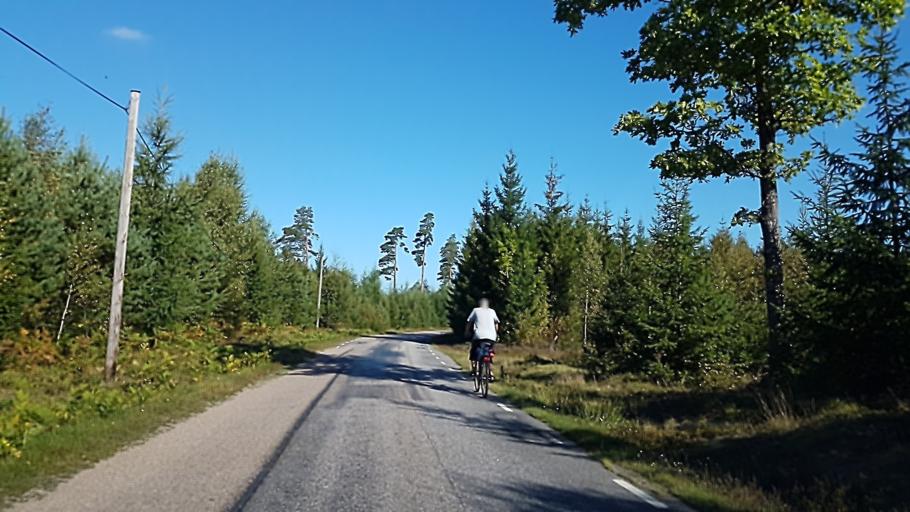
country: SE
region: Kronoberg
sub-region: Ljungby Kommun
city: Ljungby
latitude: 56.8066
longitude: 14.0328
